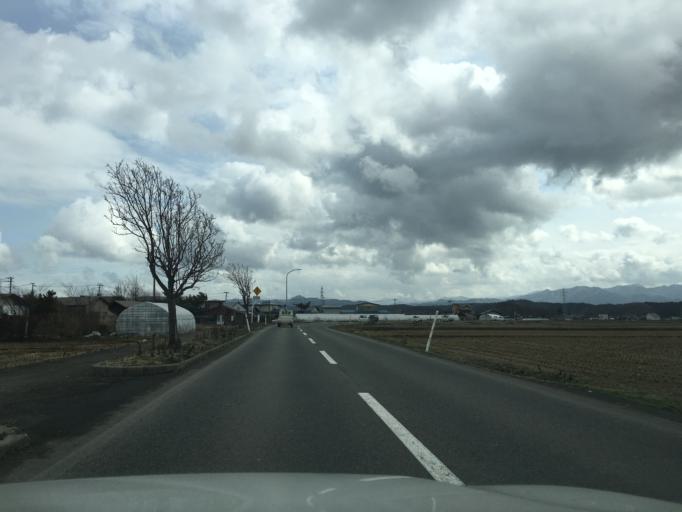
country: JP
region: Akita
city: Tenno
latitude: 39.9362
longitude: 140.0905
